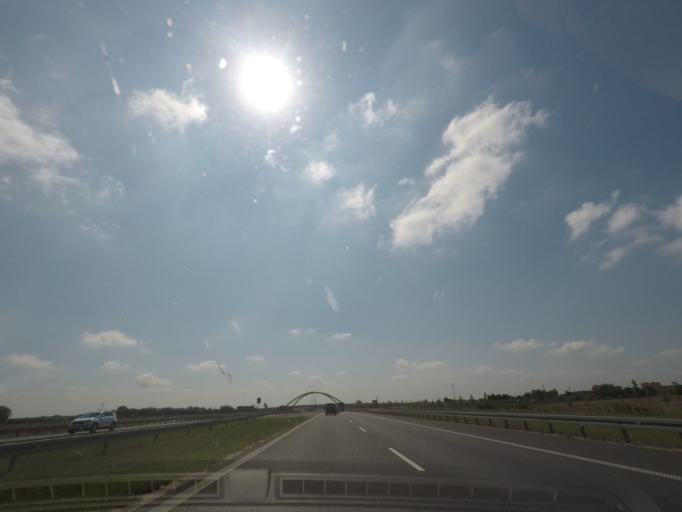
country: PL
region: Kujawsko-Pomorskie
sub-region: Powiat wloclawski
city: Chocen
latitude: 52.5737
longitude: 19.0053
